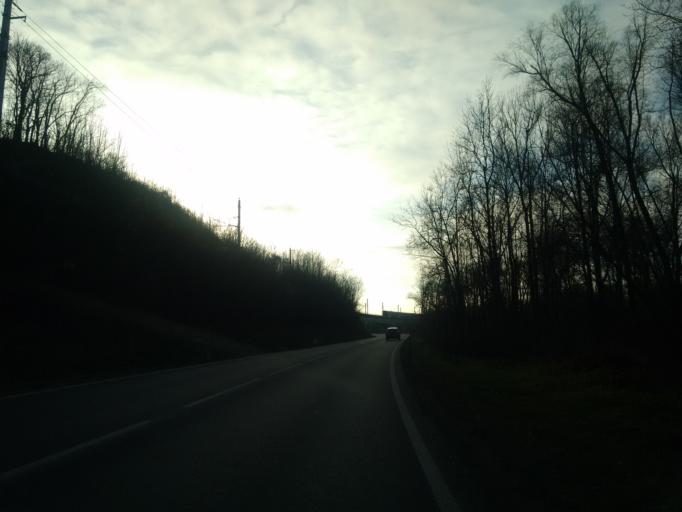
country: AT
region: Lower Austria
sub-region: Politischer Bezirk Melk
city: Melk
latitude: 48.2218
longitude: 15.3199
